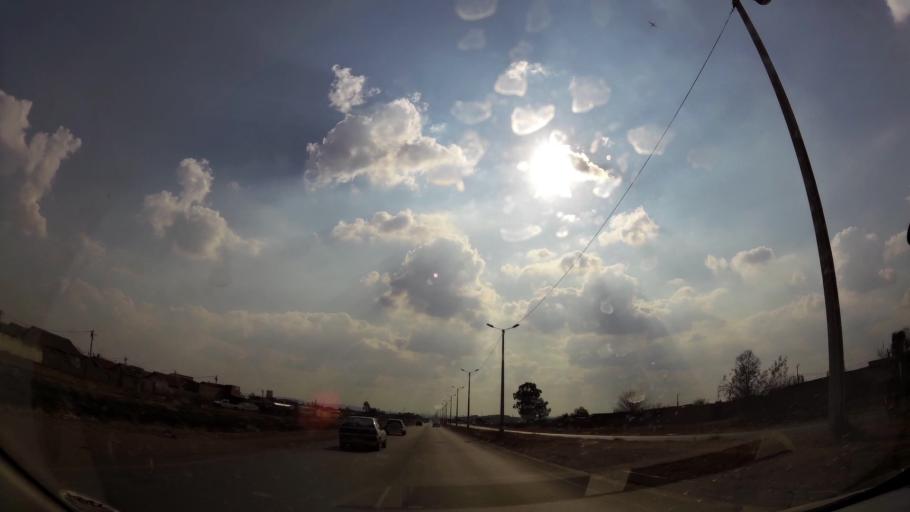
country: ZA
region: Gauteng
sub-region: Ekurhuleni Metropolitan Municipality
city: Germiston
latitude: -26.3139
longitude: 28.2059
